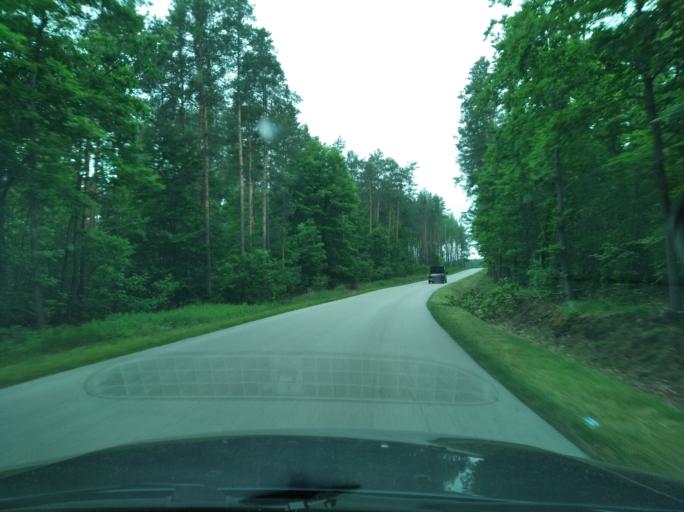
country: PL
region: Subcarpathian Voivodeship
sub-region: Powiat kolbuszowski
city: Niwiska
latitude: 50.2106
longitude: 21.6367
